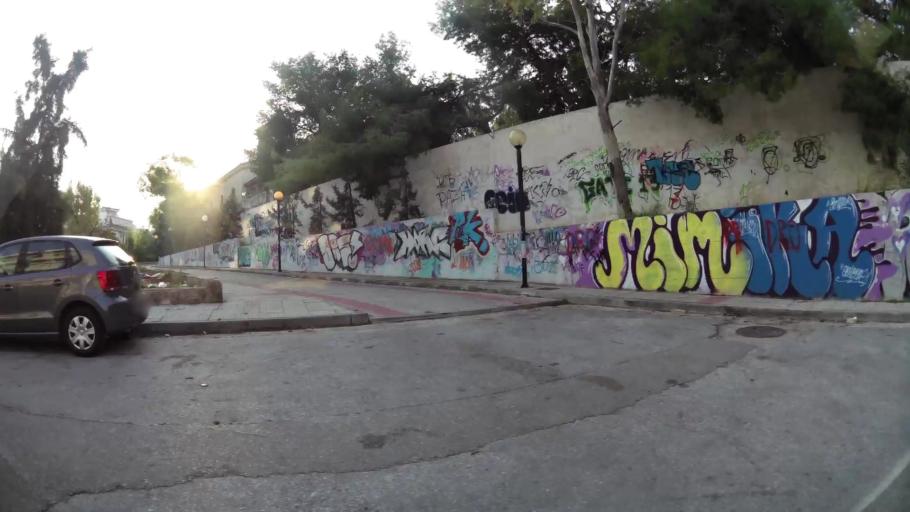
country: GR
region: Attica
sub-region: Nomarchia Athinas
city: Agios Dimitrios
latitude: 37.9400
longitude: 23.7272
